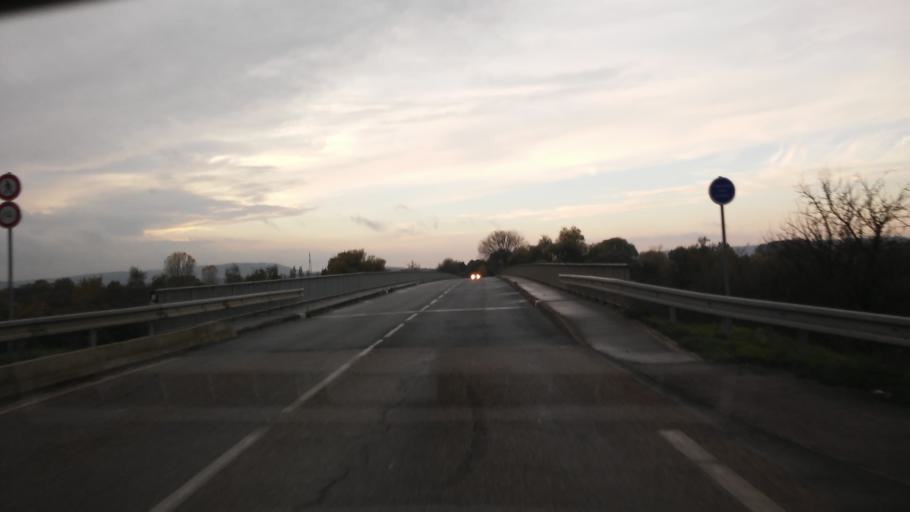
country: FR
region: Lorraine
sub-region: Departement de la Moselle
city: Ay-sur-Moselle
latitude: 49.2414
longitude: 6.1927
